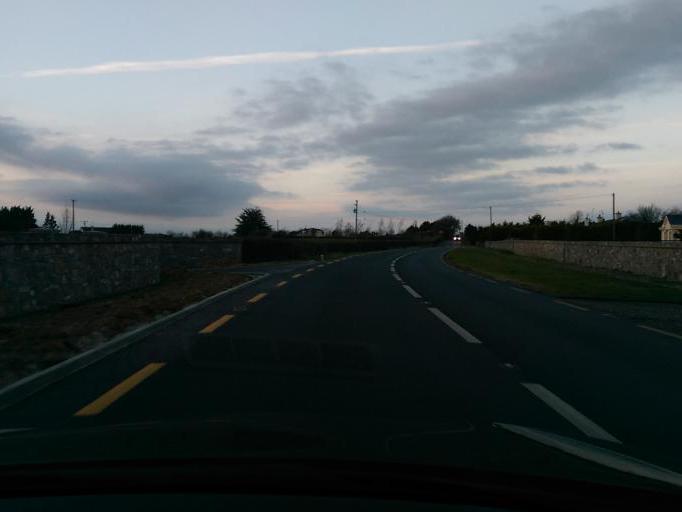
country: IE
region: Munster
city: Nenagh Bridge
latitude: 52.9782
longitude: -8.1315
